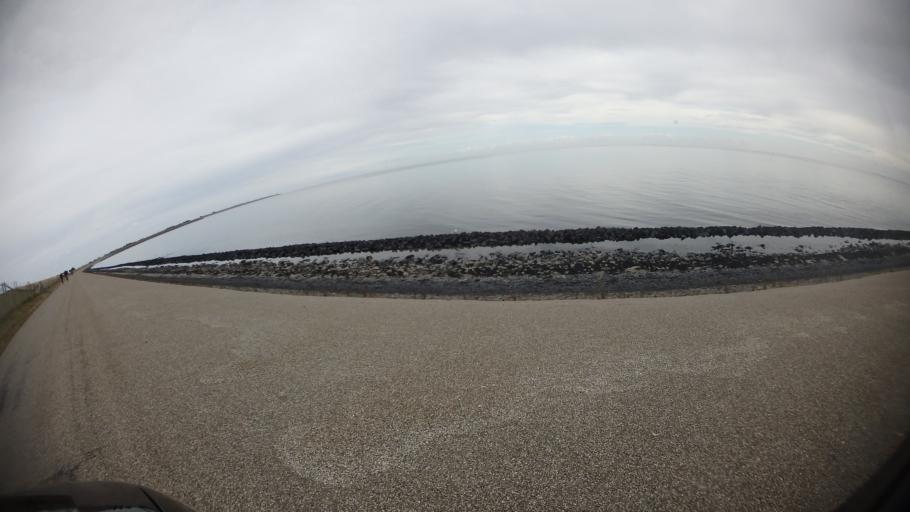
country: NL
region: North Holland
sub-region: Gemeente Texel
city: Den Burg
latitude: 53.0578
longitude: 4.8732
